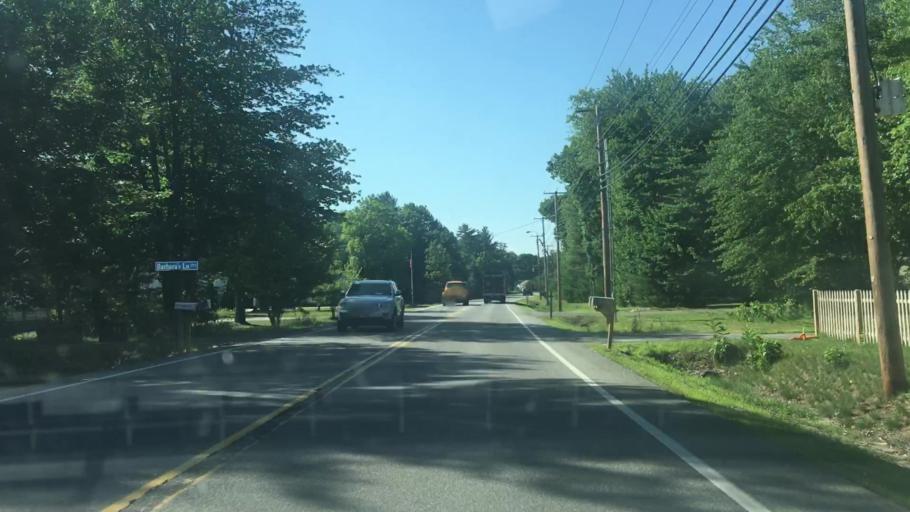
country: US
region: Maine
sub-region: York County
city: Biddeford
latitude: 43.5495
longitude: -70.4903
